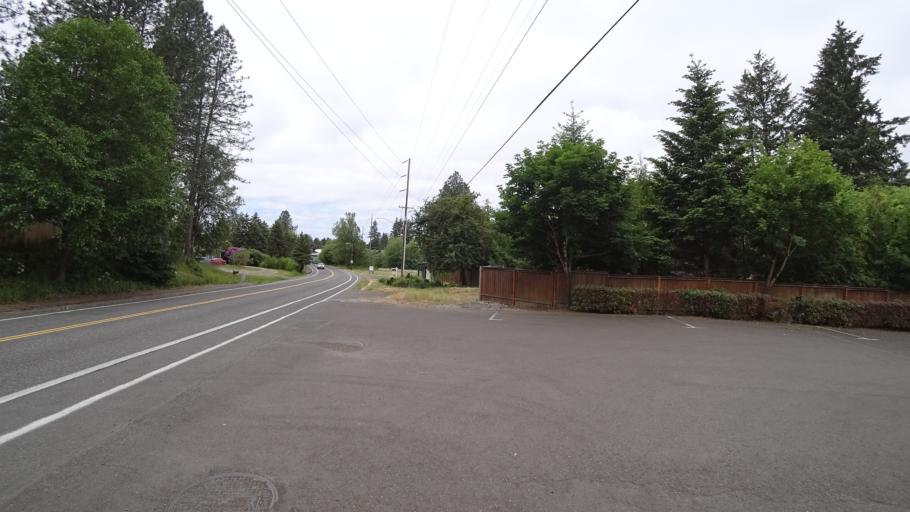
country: US
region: Oregon
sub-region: Washington County
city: Garden Home-Whitford
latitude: 45.4674
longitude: -122.7455
